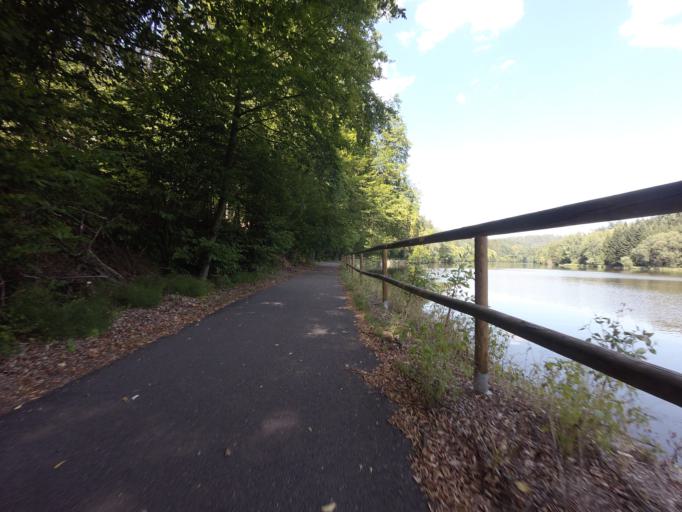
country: CZ
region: Jihocesky
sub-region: Okres Ceske Budejovice
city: Hluboka nad Vltavou
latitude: 49.0789
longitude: 14.4551
